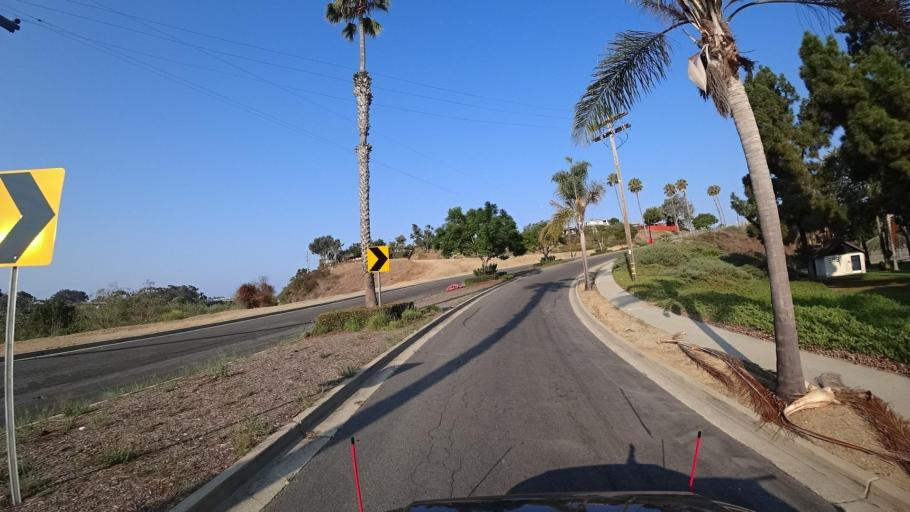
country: US
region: California
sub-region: San Diego County
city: Oceanside
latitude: 33.2109
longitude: -117.3808
